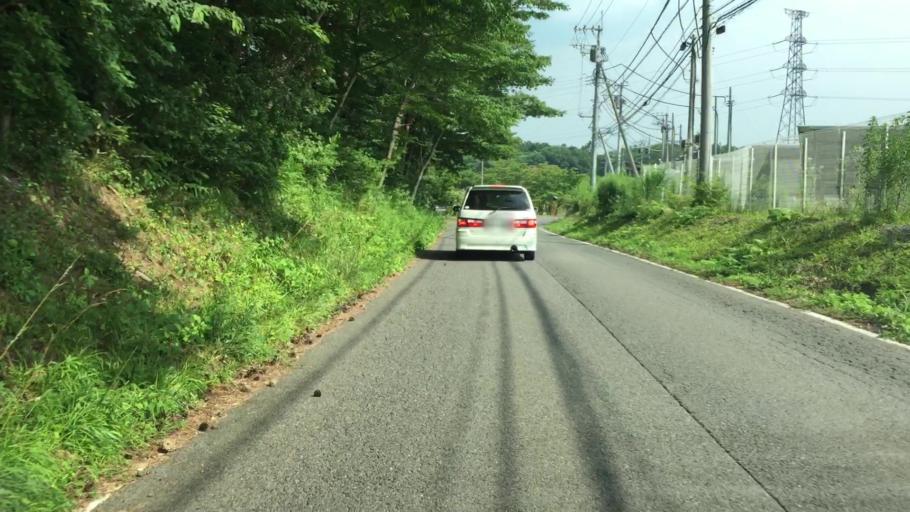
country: JP
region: Tochigi
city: Kuroiso
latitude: 37.0529
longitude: 139.9444
